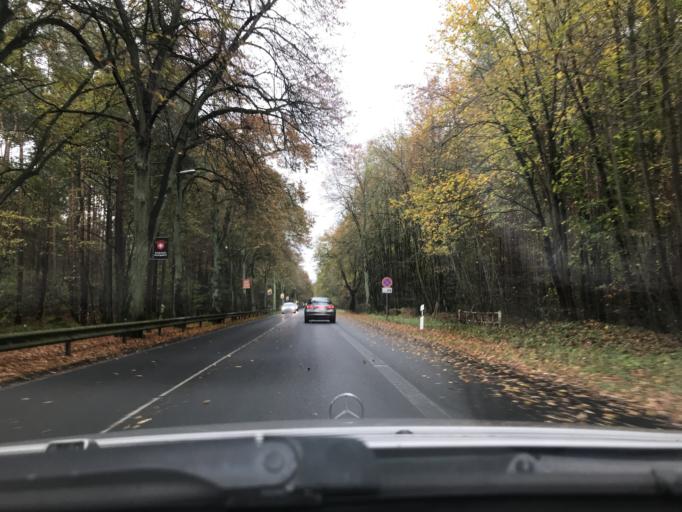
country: DE
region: Mecklenburg-Vorpommern
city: Seebad Heringsdorf
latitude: 53.9287
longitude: 14.2031
